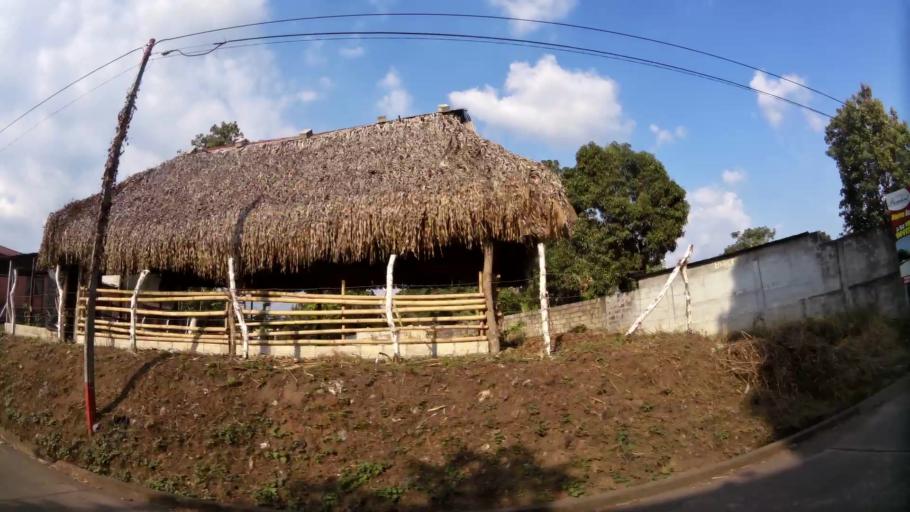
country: GT
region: Retalhuleu
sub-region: Municipio de Retalhuleu
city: Retalhuleu
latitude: 14.5330
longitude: -91.6731
